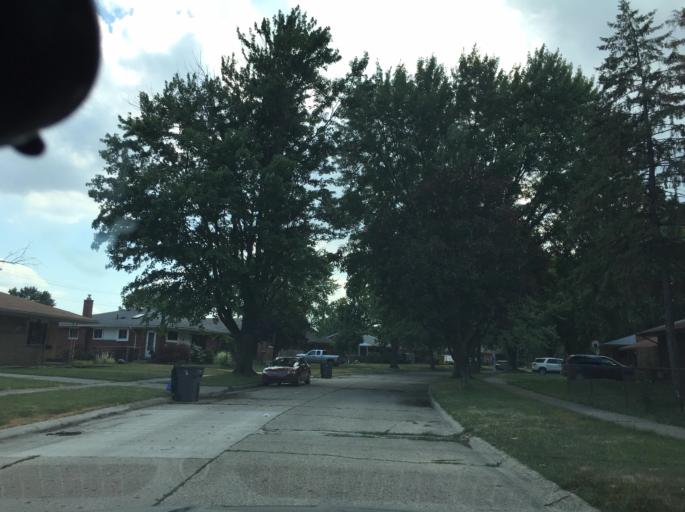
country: US
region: Michigan
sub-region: Macomb County
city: Clinton
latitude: 42.5599
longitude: -82.9058
